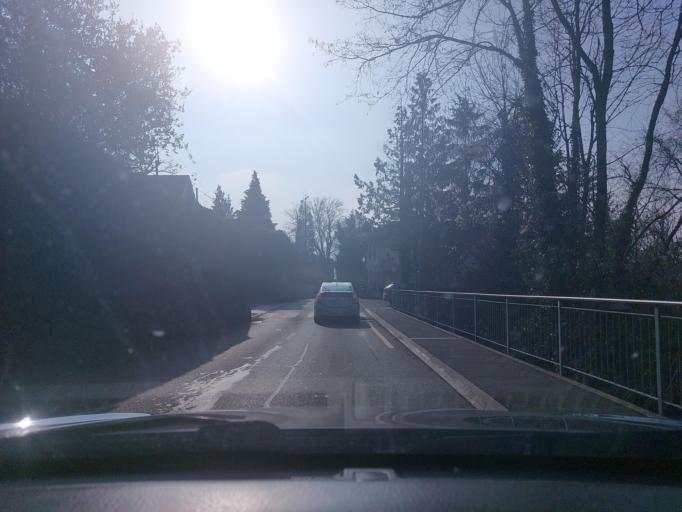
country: CH
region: Vaud
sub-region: Lavaux-Oron District
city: Paudex
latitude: 46.5108
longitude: 6.6731
